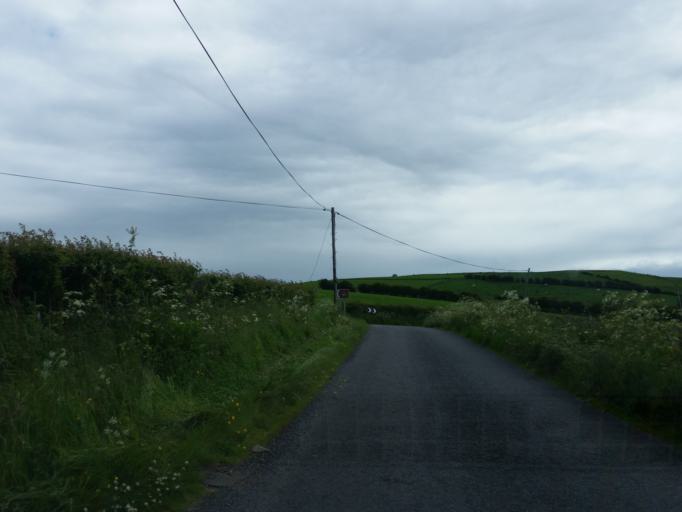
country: GB
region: Northern Ireland
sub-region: Omagh District
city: Omagh
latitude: 54.5314
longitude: -7.1385
